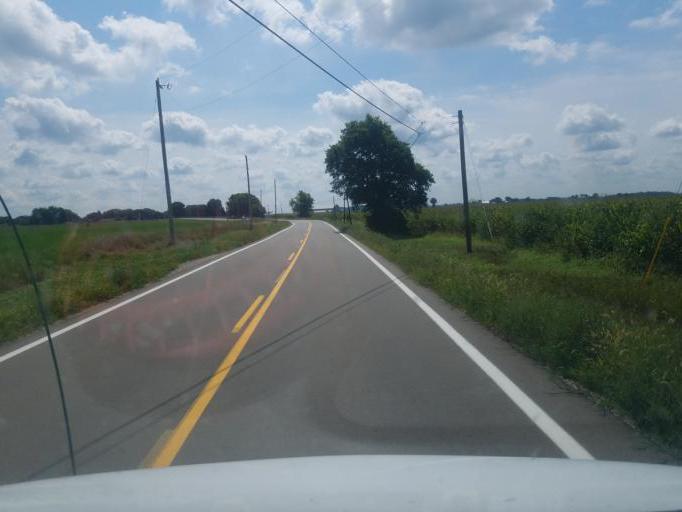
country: US
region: Ohio
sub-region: Marion County
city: Prospect
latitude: 40.3970
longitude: -83.1619
